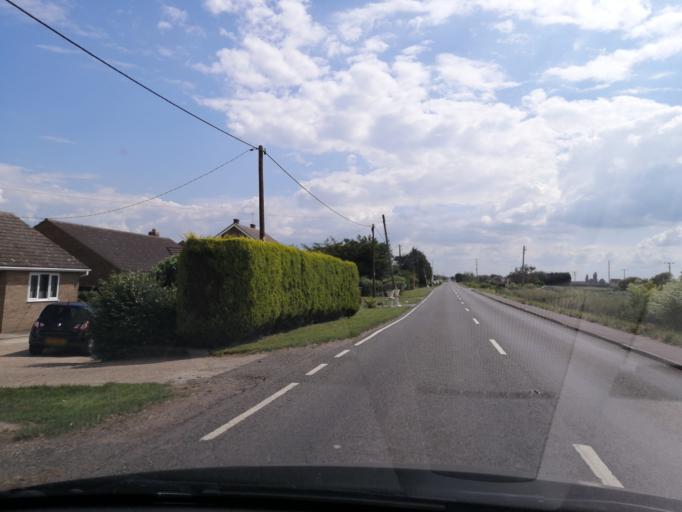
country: GB
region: England
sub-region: Cambridgeshire
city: Ramsey
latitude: 52.4902
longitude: -0.1486
